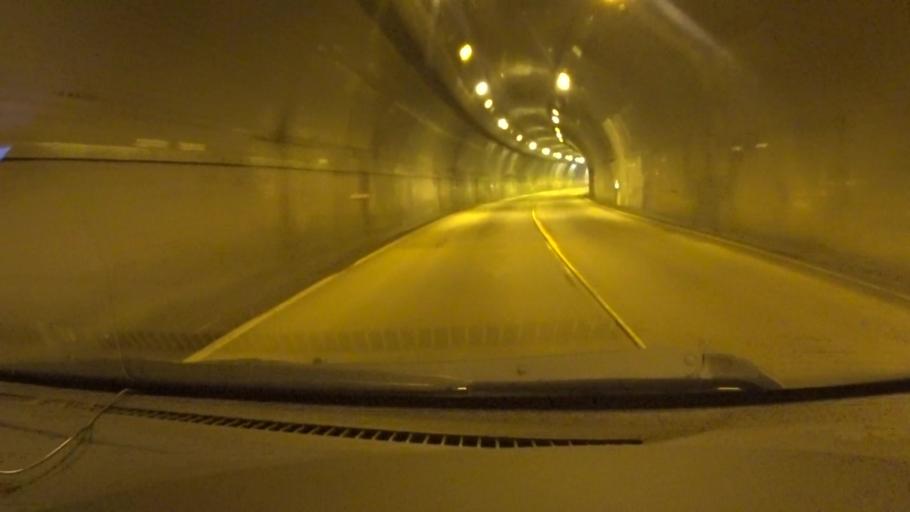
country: JP
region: Kyoto
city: Maizuru
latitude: 35.4868
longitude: 135.4689
